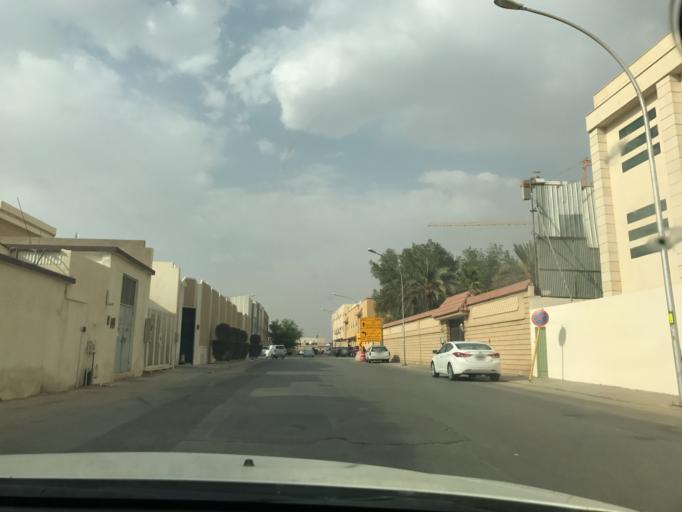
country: SA
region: Ar Riyad
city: Riyadh
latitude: 24.7065
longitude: 46.7108
